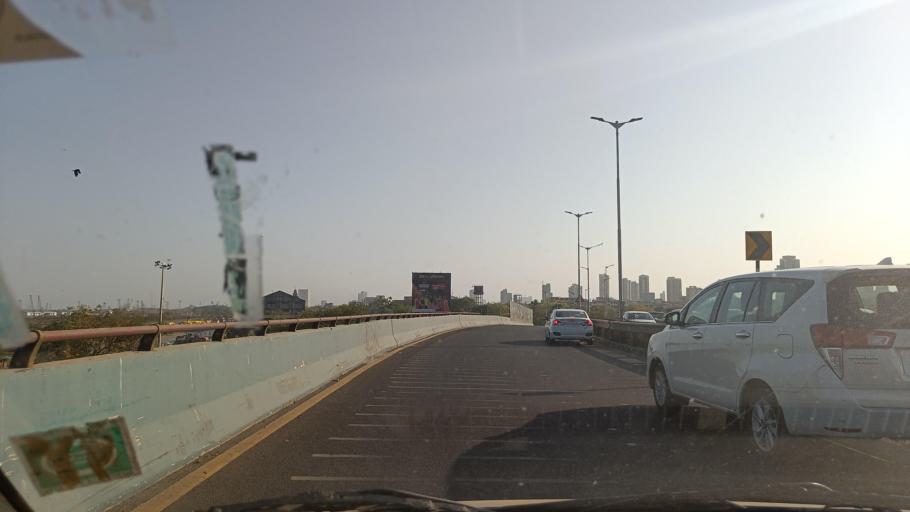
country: IN
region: Maharashtra
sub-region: Mumbai Suburban
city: Mumbai
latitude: 18.9609
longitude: 72.8442
